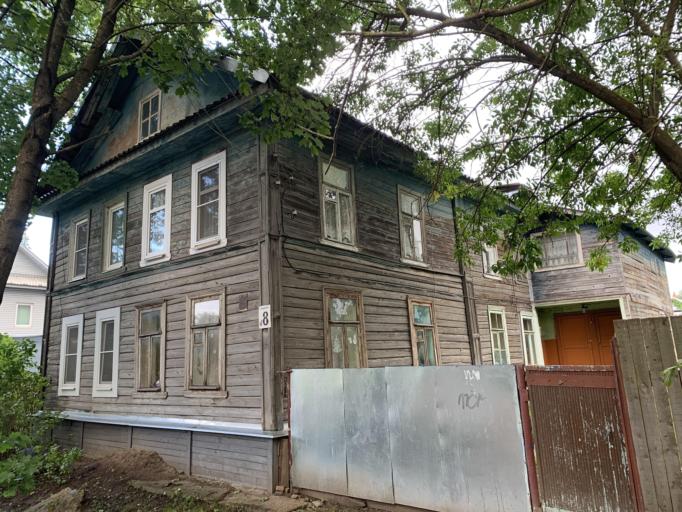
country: RU
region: Tverskaya
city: Vyshniy Volochek
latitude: 57.5833
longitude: 34.5499
